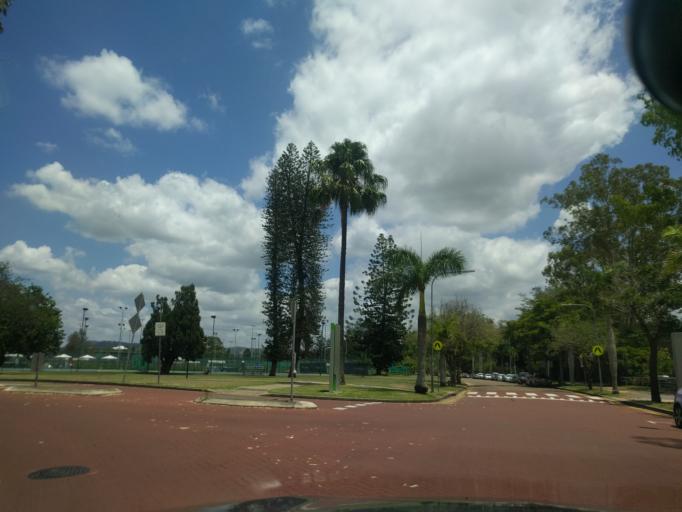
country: AU
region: Queensland
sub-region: Brisbane
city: South Brisbane
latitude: -27.4944
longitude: 153.0169
